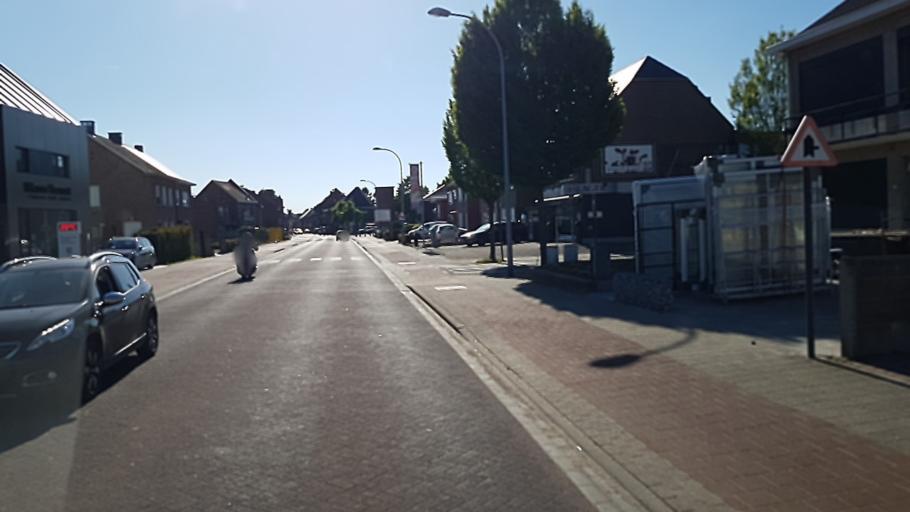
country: BE
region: Flanders
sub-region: Provincie Antwerpen
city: Herenthout
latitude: 51.1407
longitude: 4.7645
